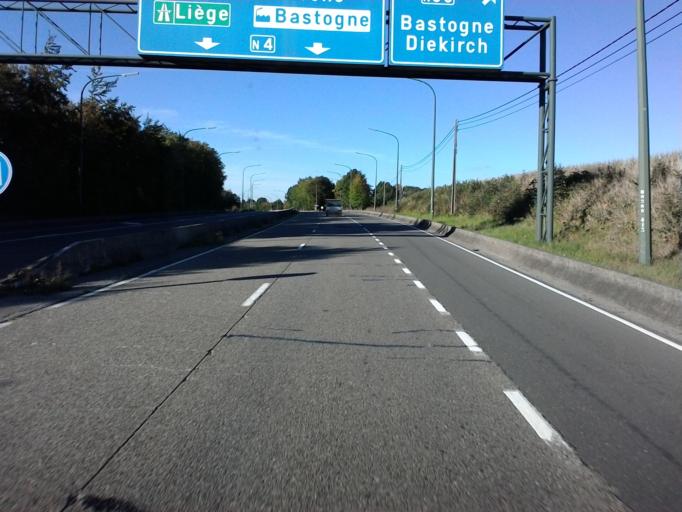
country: BE
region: Wallonia
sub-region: Province du Luxembourg
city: Bastogne
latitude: 49.9792
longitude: 5.7195
